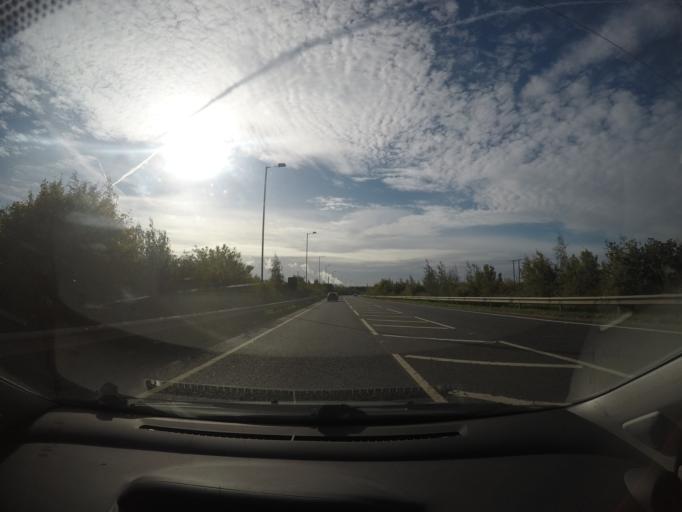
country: GB
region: England
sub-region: North Yorkshire
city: Barlby
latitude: 53.7858
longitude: -1.0377
